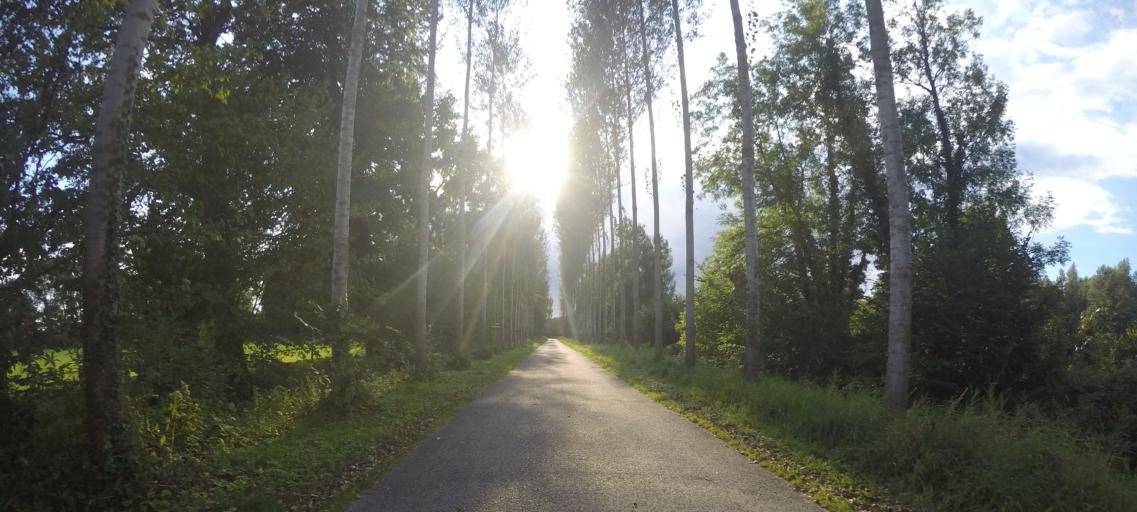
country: DE
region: North Rhine-Westphalia
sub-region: Regierungsbezirk Arnsberg
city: Lippstadt
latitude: 51.6943
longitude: 8.3344
